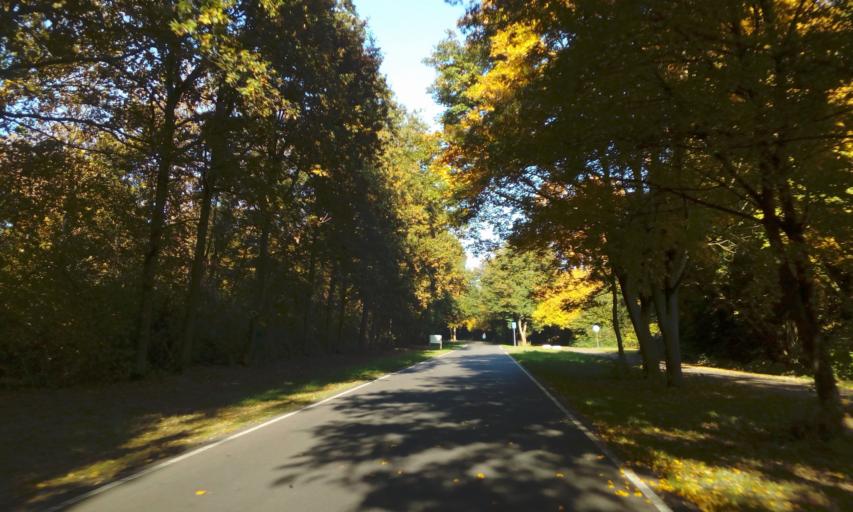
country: NL
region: South Holland
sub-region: Gemeente Lansingerland
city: Bleiswijk
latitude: 52.0024
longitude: 4.5456
